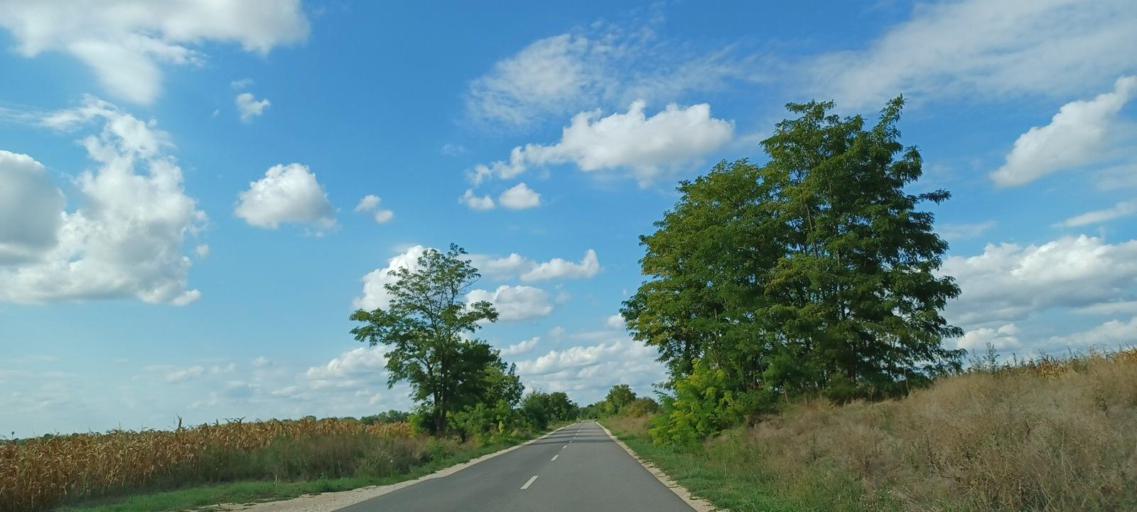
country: HU
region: Tolna
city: Zomba
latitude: 46.4473
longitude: 18.6051
